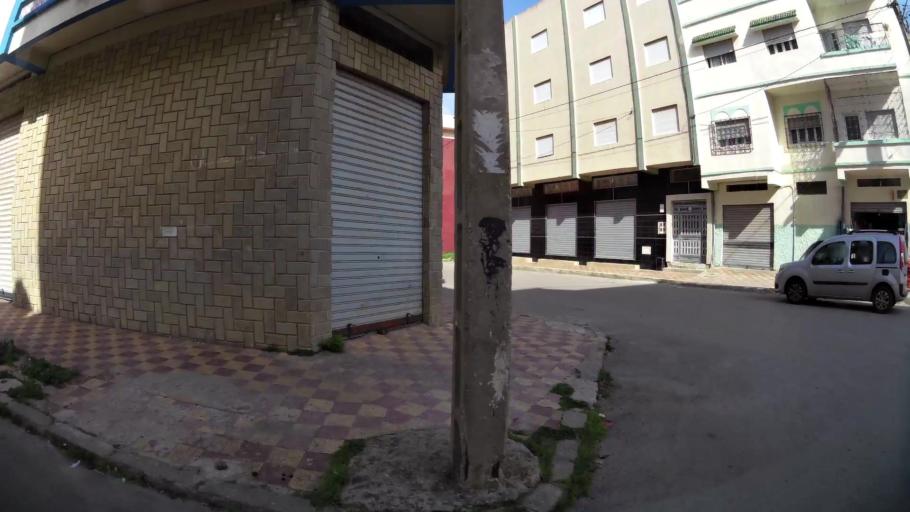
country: MA
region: Tanger-Tetouan
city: Tetouan
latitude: 35.5904
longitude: -5.3519
